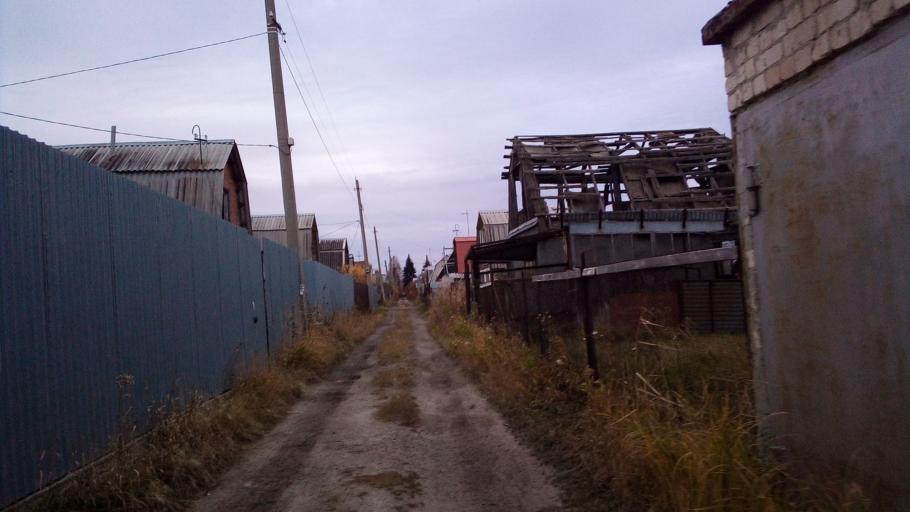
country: RU
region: Chelyabinsk
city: Novosineglazovskiy
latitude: 54.9844
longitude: 61.4031
